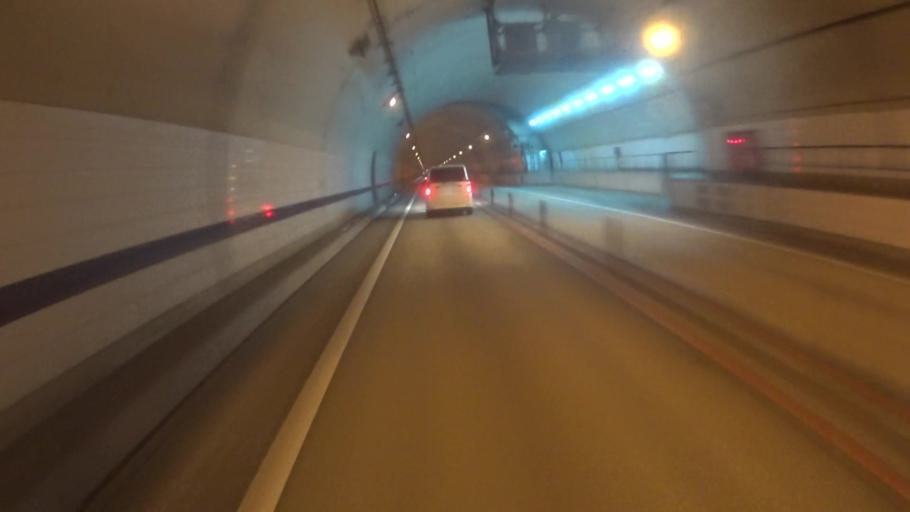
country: JP
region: Kyoto
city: Miyazu
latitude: 35.4785
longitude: 135.1753
